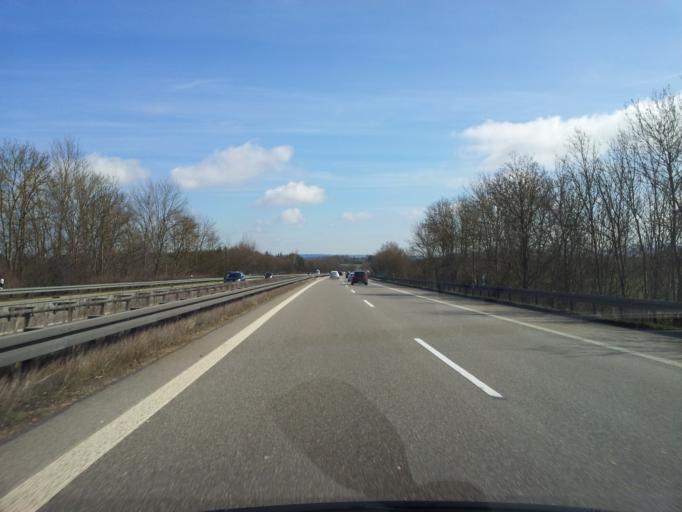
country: DE
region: Baden-Wuerttemberg
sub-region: Freiburg Region
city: Villingendorf
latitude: 48.1959
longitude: 8.5941
